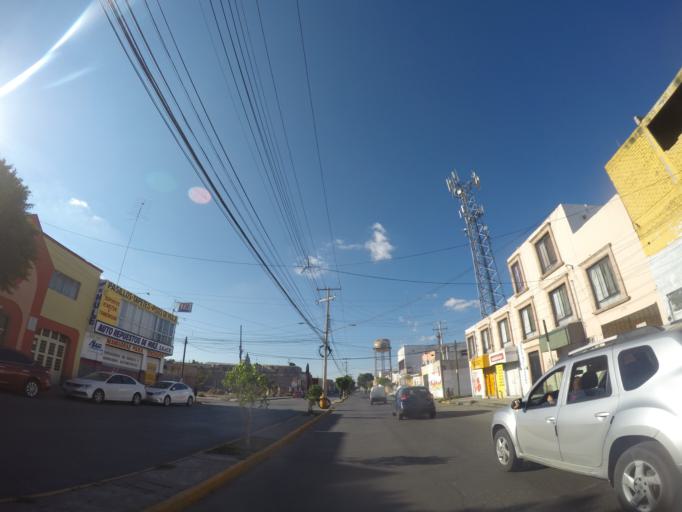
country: MX
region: San Luis Potosi
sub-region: San Luis Potosi
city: San Luis Potosi
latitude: 22.1611
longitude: -100.9800
